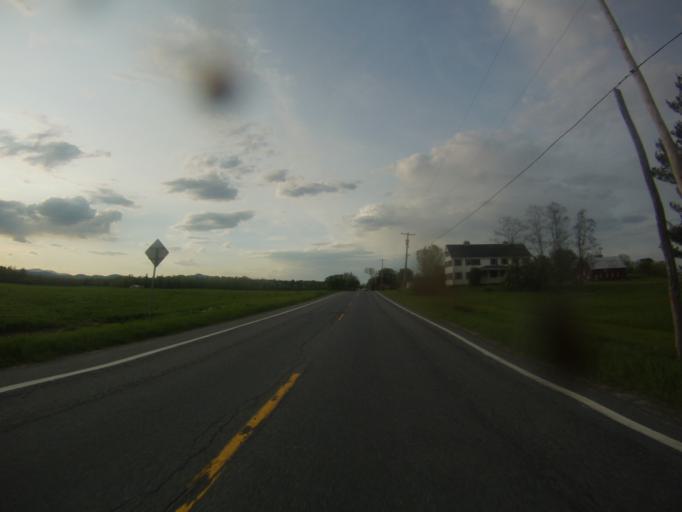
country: US
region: New York
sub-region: Essex County
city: Port Henry
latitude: 44.0029
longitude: -73.4194
